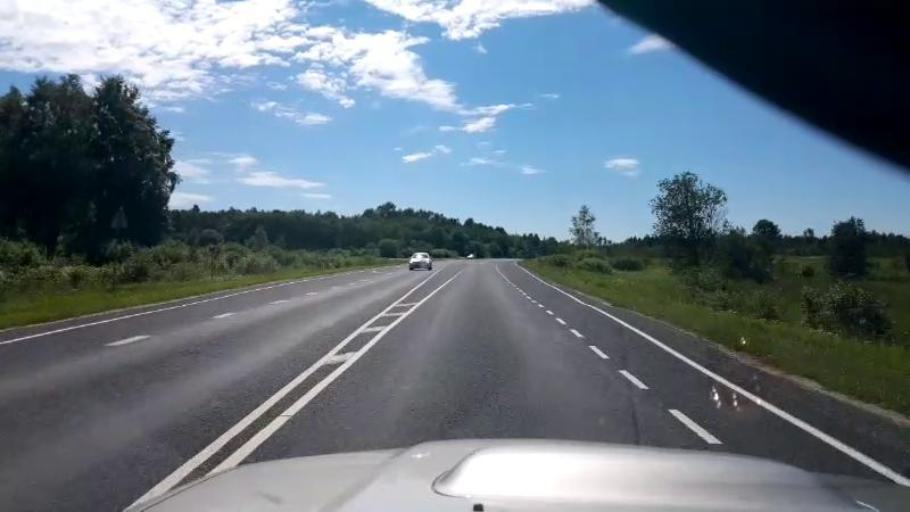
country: EE
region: Jaervamaa
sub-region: Jaerva-Jaani vald
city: Jarva-Jaani
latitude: 59.0498
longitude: 25.8807
